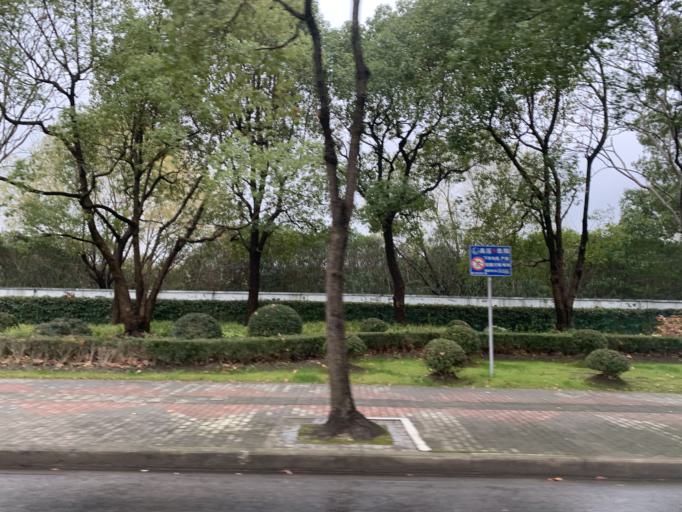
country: CN
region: Shanghai Shi
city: Huamu
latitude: 31.1959
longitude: 121.5405
